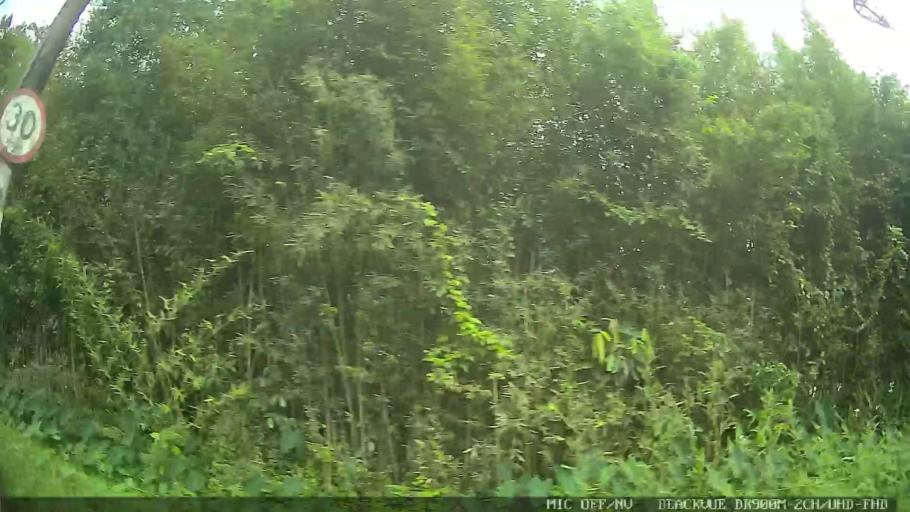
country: BR
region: Sao Paulo
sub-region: Bertioga
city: Bertioga
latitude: -23.8004
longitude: -46.0579
